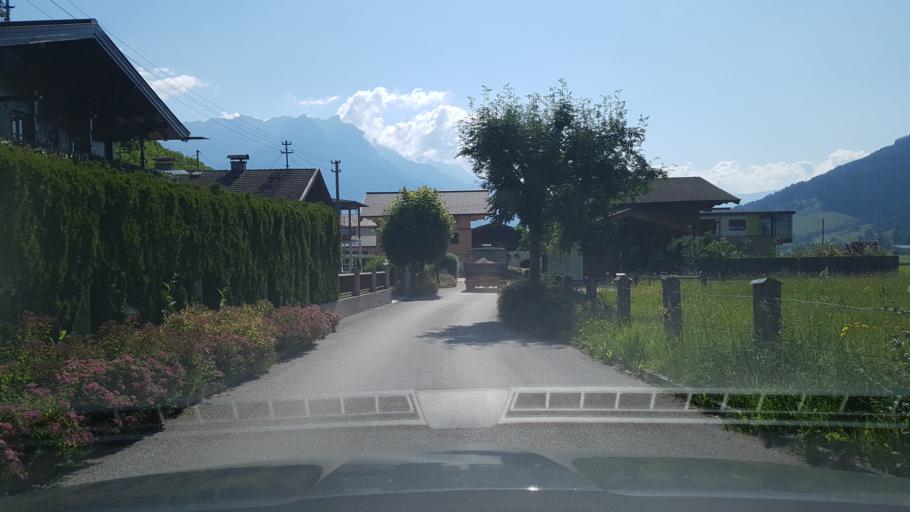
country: AT
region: Salzburg
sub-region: Politischer Bezirk Zell am See
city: Leogang
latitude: 47.4452
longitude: 12.7762
